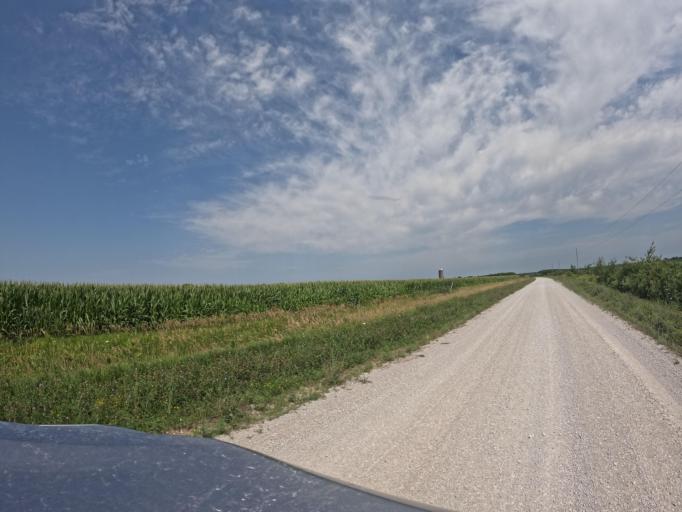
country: US
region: Iowa
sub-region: Appanoose County
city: Centerville
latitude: 40.8154
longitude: -92.9447
